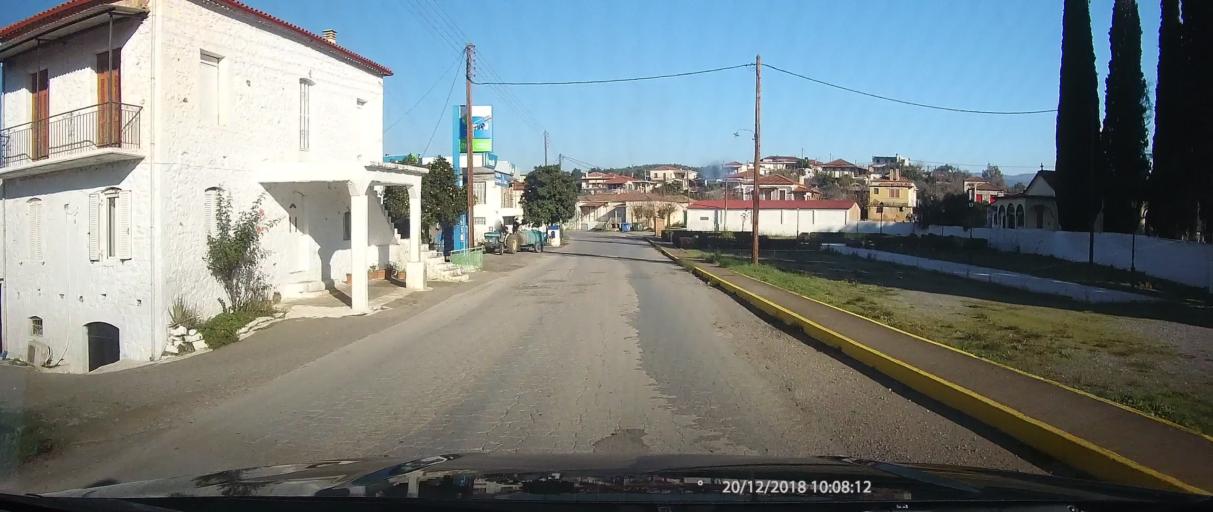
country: GR
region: Peloponnese
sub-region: Nomos Lakonias
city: Sparti
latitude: 37.0161
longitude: 22.4894
